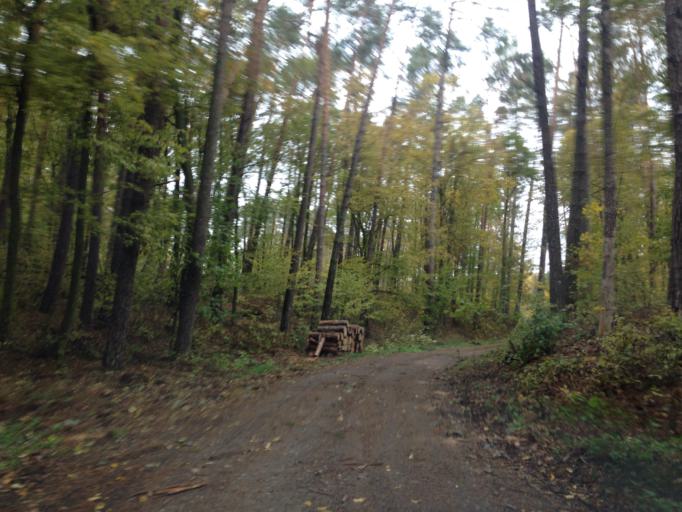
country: PL
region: Kujawsko-Pomorskie
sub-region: Powiat brodnicki
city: Gorzno
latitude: 53.2562
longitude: 19.6896
